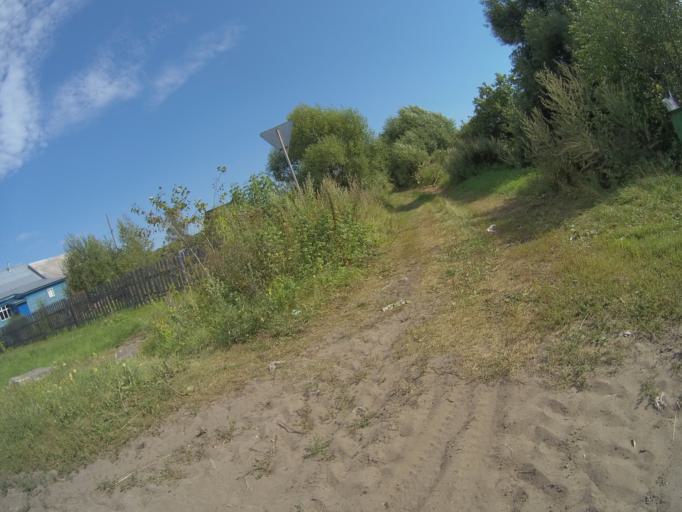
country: RU
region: Vladimir
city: Orgtrud
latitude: 56.0334
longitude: 40.6782
